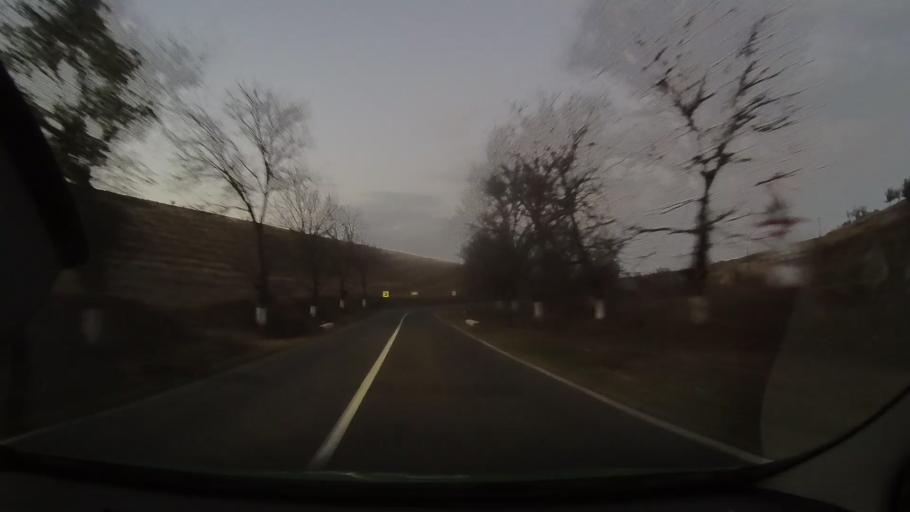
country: RO
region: Constanta
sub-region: Comuna Ion Corvin
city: Ion Corvin
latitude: 44.1025
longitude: 27.7550
